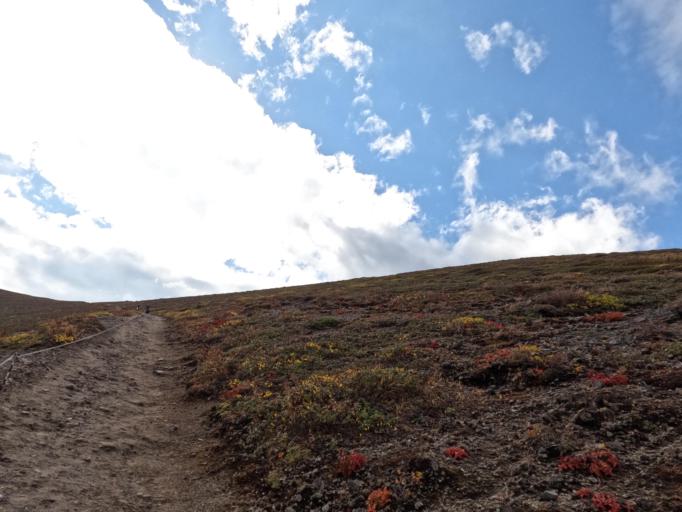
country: JP
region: Hokkaido
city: Shiraoi
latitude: 42.6911
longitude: 141.3892
